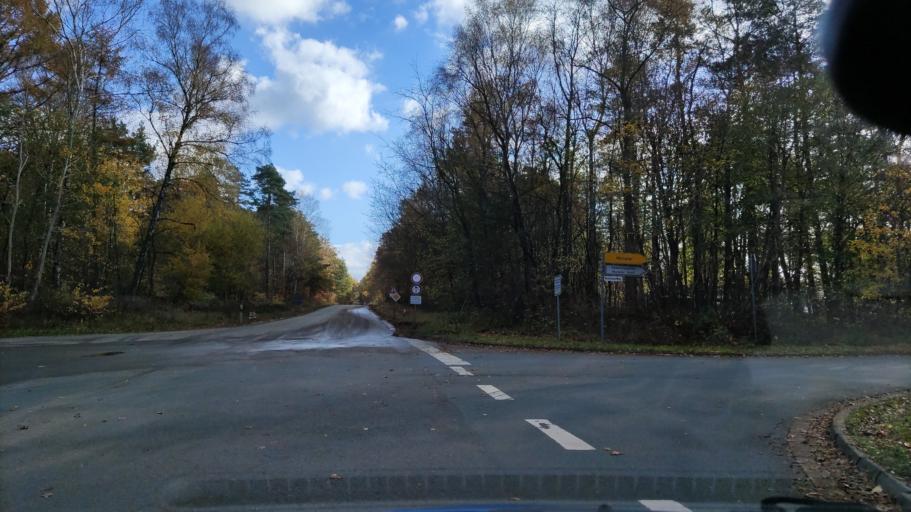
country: DE
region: Lower Saxony
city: Munster
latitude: 53.0030
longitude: 10.1186
